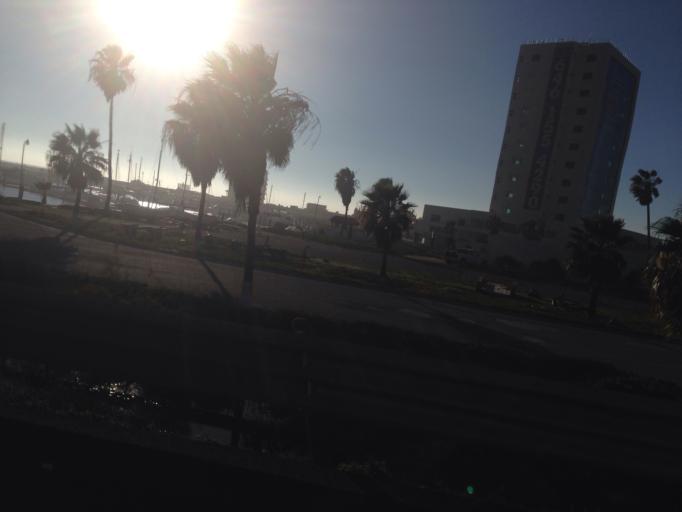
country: MX
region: Baja California
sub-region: Playas de Rosarito
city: Santa Anita
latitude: 32.0571
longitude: -116.8774
